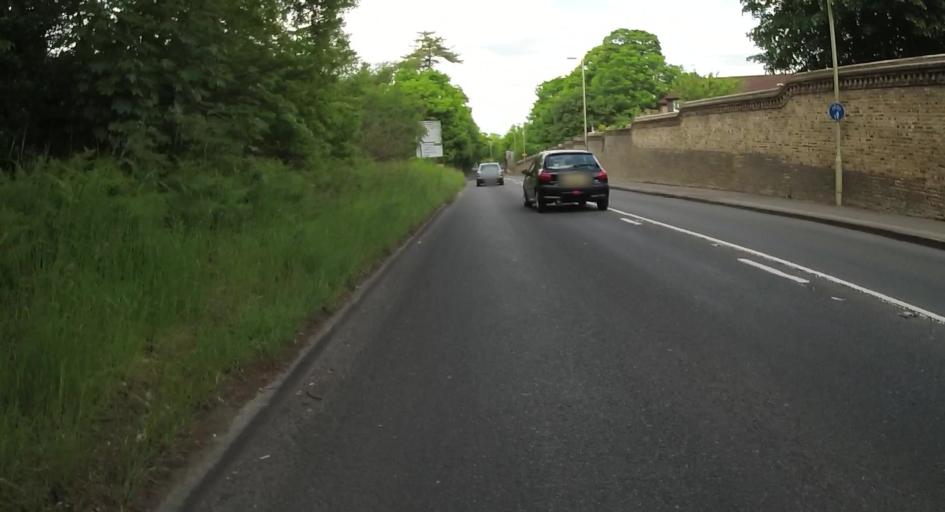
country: GB
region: England
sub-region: Hampshire
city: Aldershot
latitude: 51.2480
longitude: -0.7815
